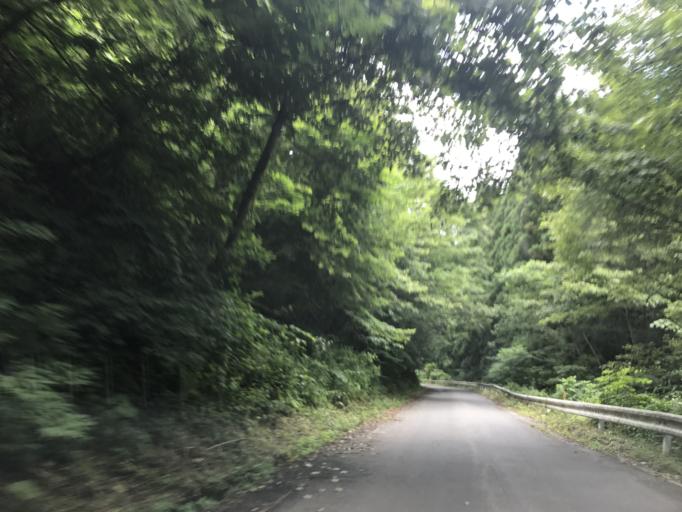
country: JP
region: Iwate
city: Ichinoseki
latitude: 38.9695
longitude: 140.9196
